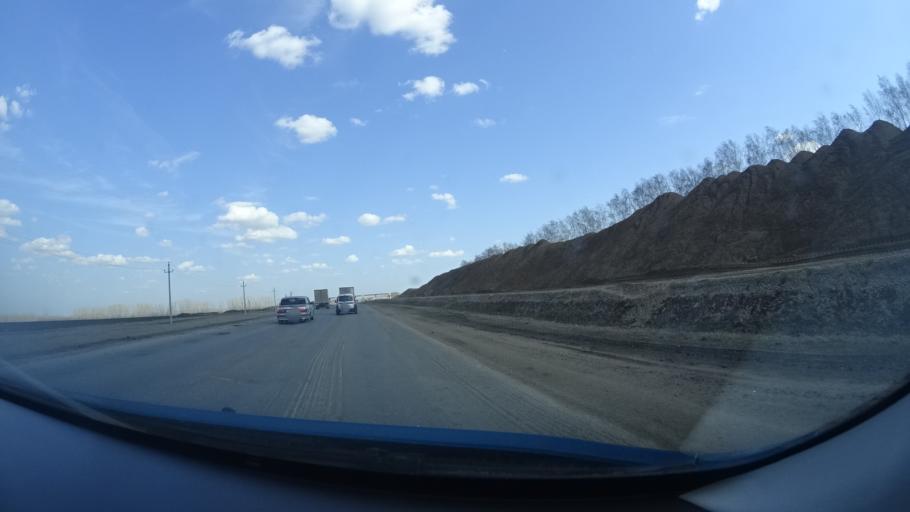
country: RU
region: Bashkortostan
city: Buzdyak
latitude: 54.6493
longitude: 54.5946
